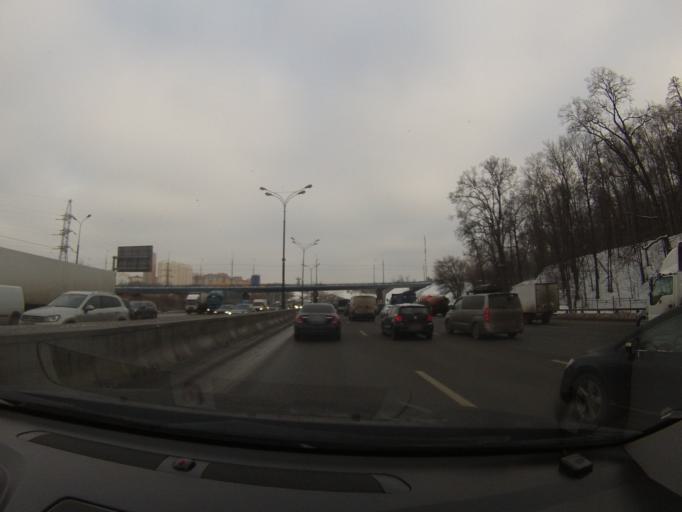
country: RU
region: Moscow
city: Strogino
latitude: 55.8505
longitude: 37.3931
